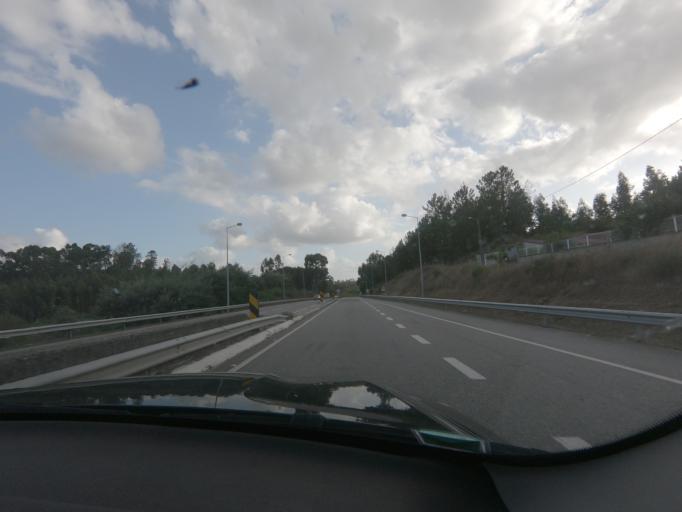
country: PT
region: Viseu
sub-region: Concelho de Tondela
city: Tondela
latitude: 40.5851
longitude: -8.0169
